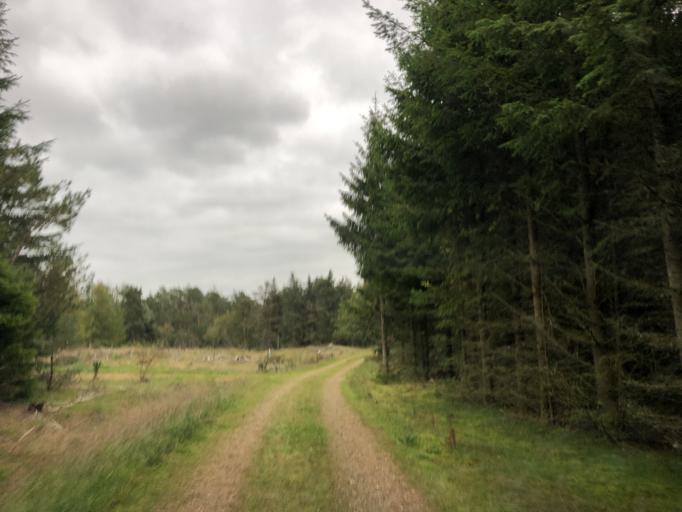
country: DK
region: Central Jutland
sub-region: Holstebro Kommune
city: Ulfborg
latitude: 56.2212
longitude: 8.4500
